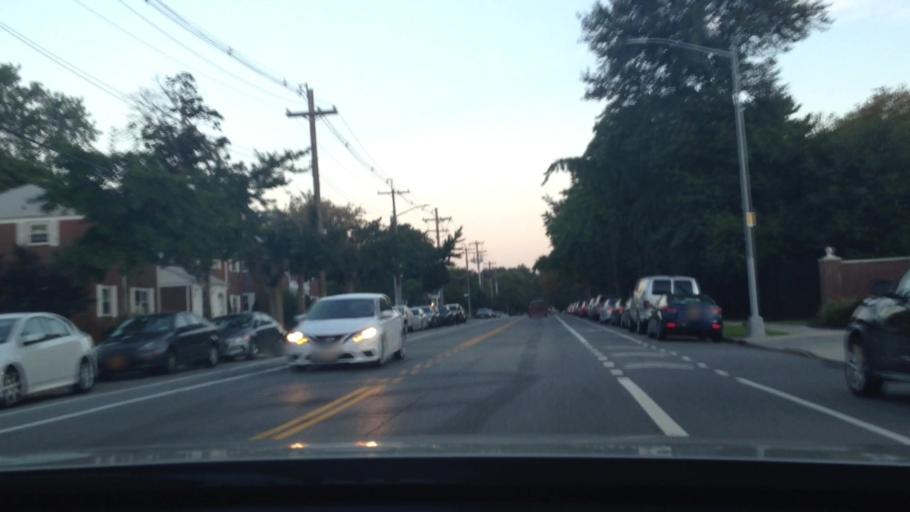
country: US
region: New York
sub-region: Nassau County
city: North New Hyde Park
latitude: 40.7496
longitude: -73.7116
